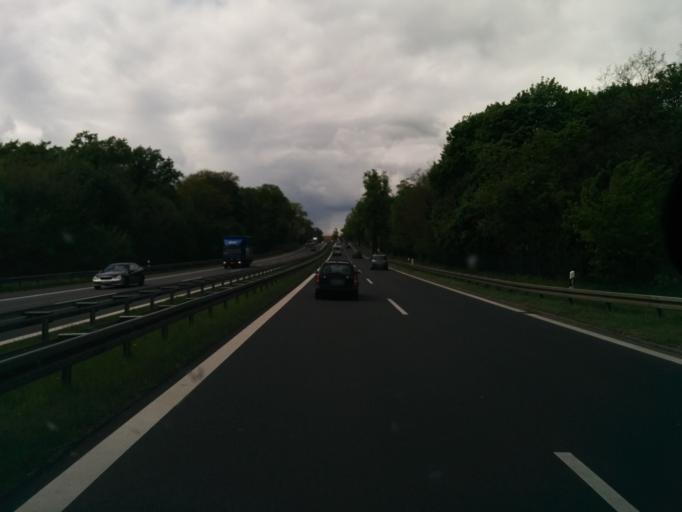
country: DE
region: Brandenburg
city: Dallgow-Doeberitz
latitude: 52.5334
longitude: 13.0167
